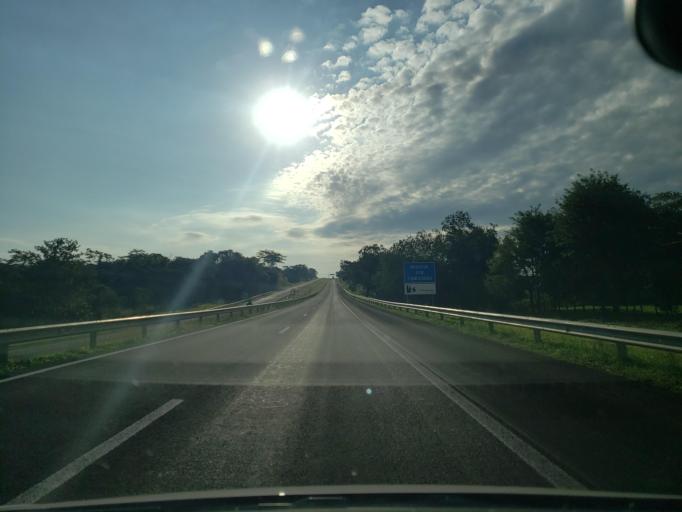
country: BR
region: Sao Paulo
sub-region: Valparaiso
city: Valparaiso
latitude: -21.1991
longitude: -50.8981
